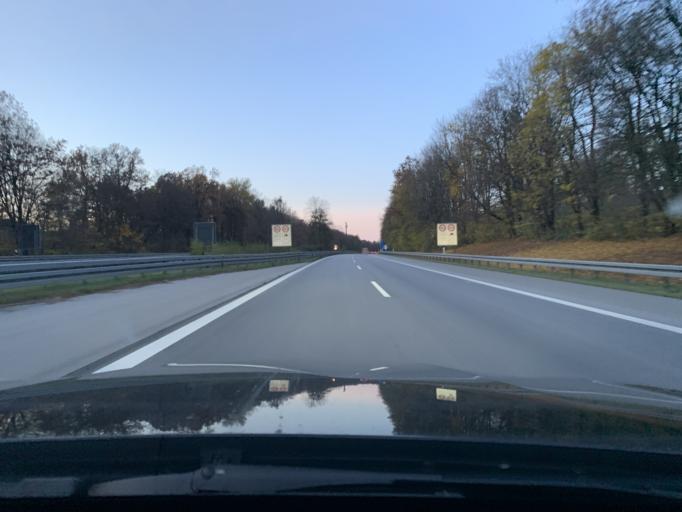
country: DE
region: Bavaria
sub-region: Upper Bavaria
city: Oberhaching
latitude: 48.0439
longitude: 11.5979
